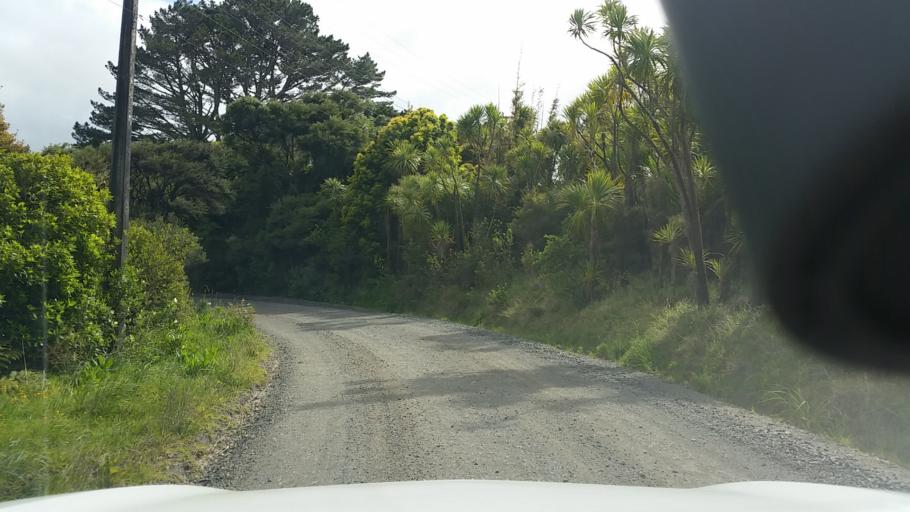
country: NZ
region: Auckland
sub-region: Auckland
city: Muriwai Beach
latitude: -36.8522
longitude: 174.4840
